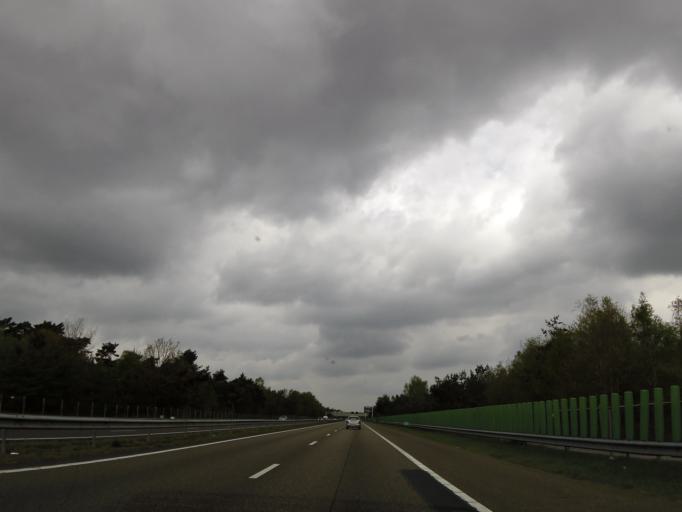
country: NL
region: North Brabant
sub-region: Gemeente Heeze-Leende
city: Heeze
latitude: 51.3718
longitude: 5.5224
